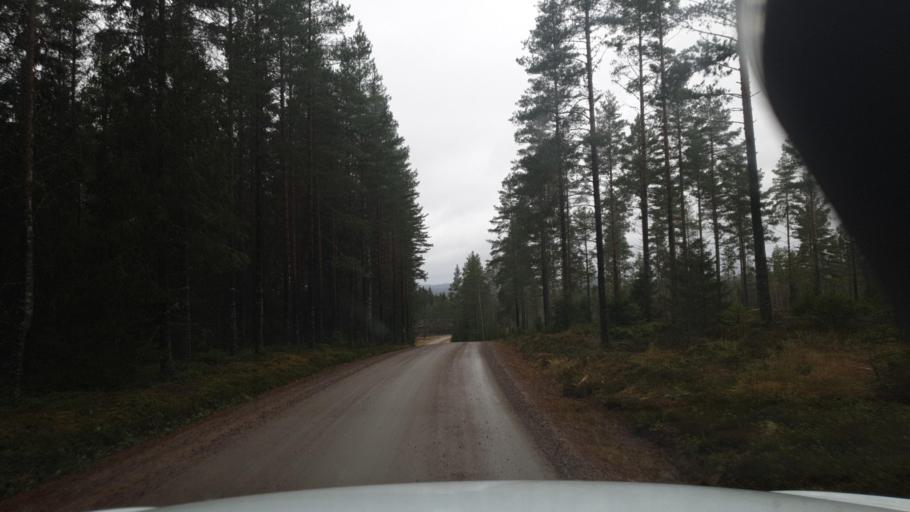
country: SE
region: Vaermland
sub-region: Arvika Kommun
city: Arvika
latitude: 59.8575
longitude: 12.6255
